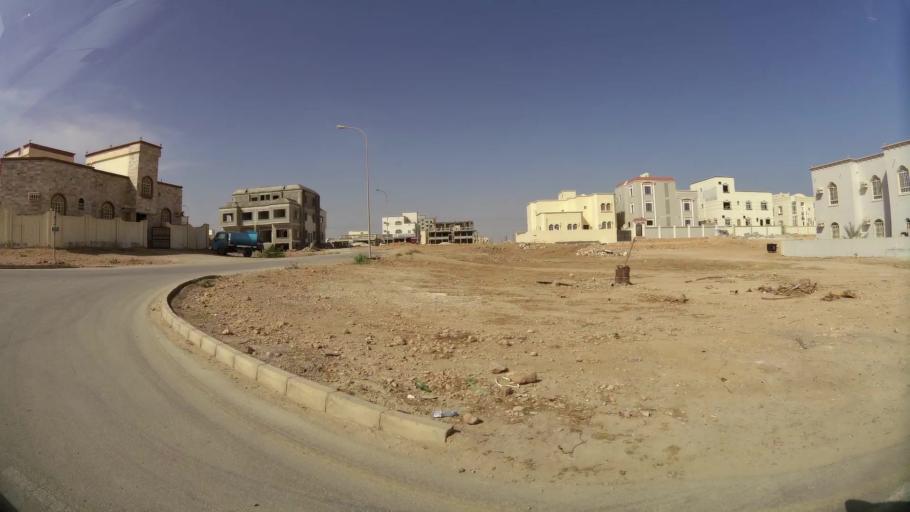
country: OM
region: Zufar
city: Salalah
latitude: 17.0061
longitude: 54.0047
